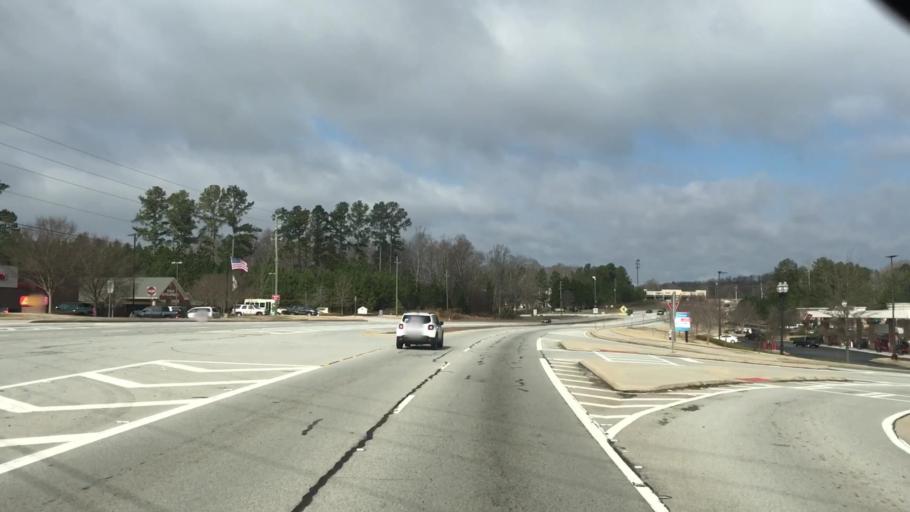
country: US
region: Georgia
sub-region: Hall County
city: Oakwood
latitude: 34.1955
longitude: -83.8589
